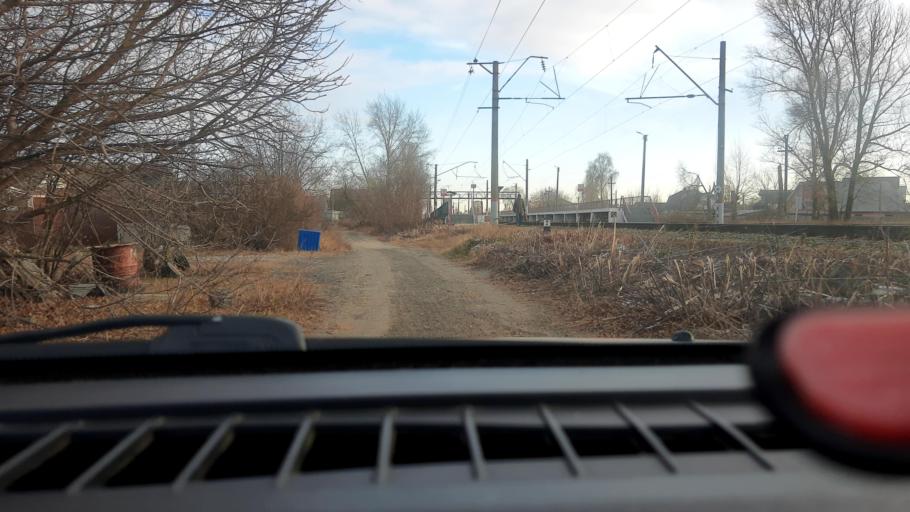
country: RU
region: Nizjnij Novgorod
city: Gorbatovka
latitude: 56.3742
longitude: 43.8087
